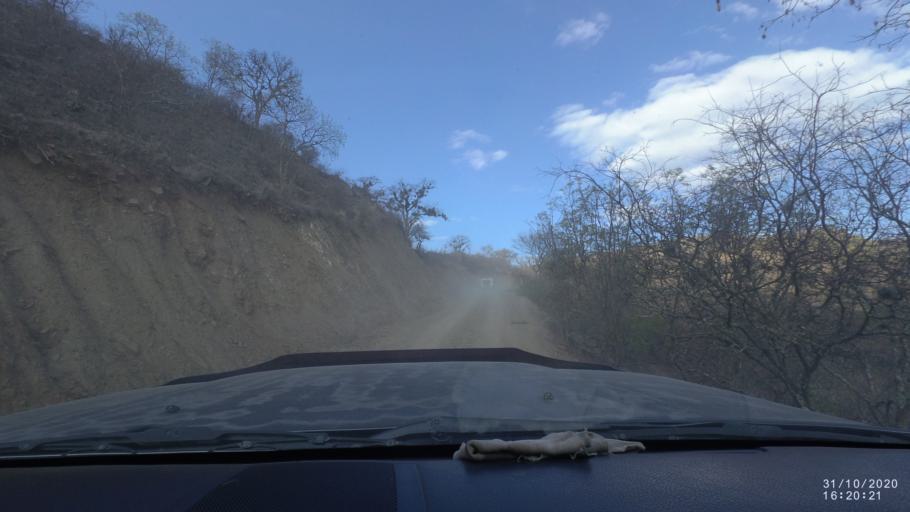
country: BO
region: Chuquisaca
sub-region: Provincia Zudanez
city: Mojocoya
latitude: -18.3979
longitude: -64.6021
